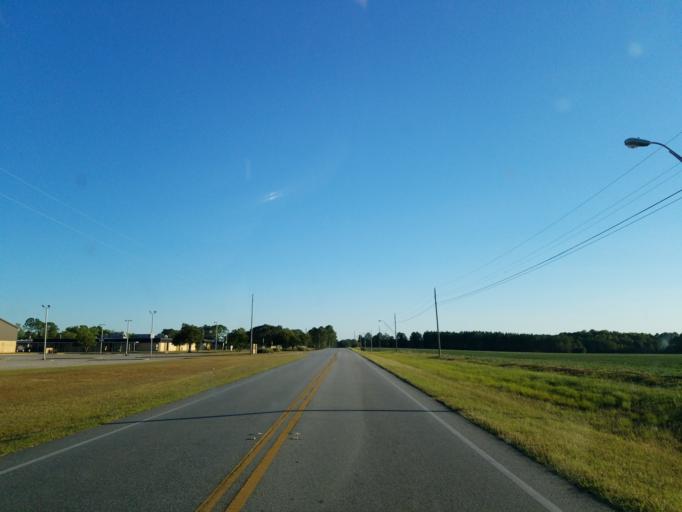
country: US
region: Georgia
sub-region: Worth County
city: Sylvester
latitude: 31.5498
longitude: -83.8430
